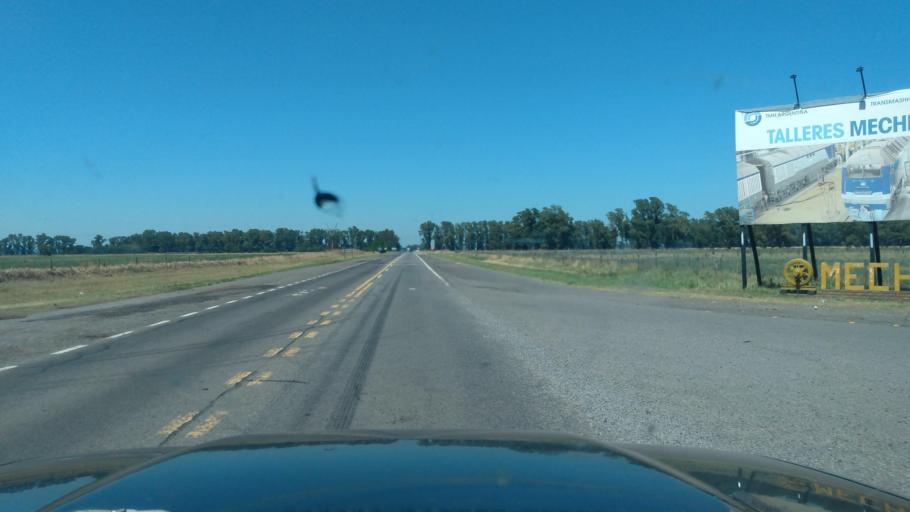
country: AR
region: Buenos Aires
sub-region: Partido de Bragado
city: Bragado
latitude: -35.0916
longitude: -60.3937
